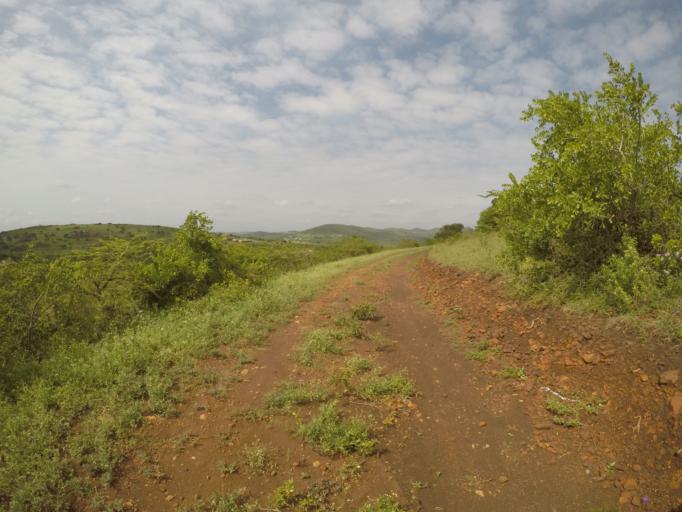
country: ZA
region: KwaZulu-Natal
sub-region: uThungulu District Municipality
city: Empangeni
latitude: -28.6183
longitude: 31.8991
